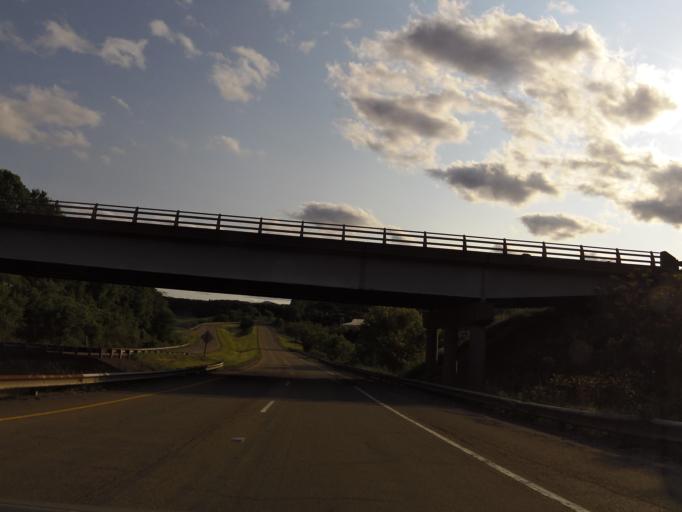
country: US
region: Virginia
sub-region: Tazewell County
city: Tazewell
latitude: 37.1280
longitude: -81.5248
